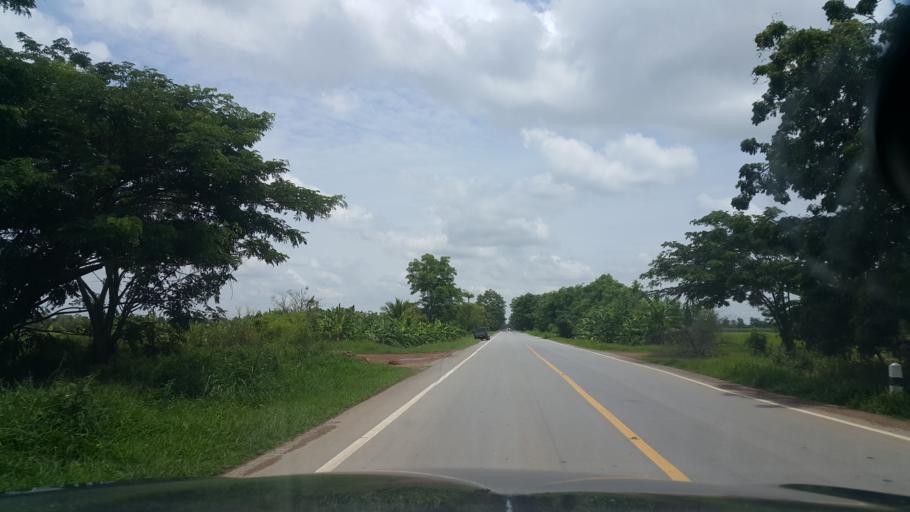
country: TH
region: Sukhothai
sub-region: Amphoe Si Satchanalai
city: Si Satchanalai
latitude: 17.3970
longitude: 99.7303
